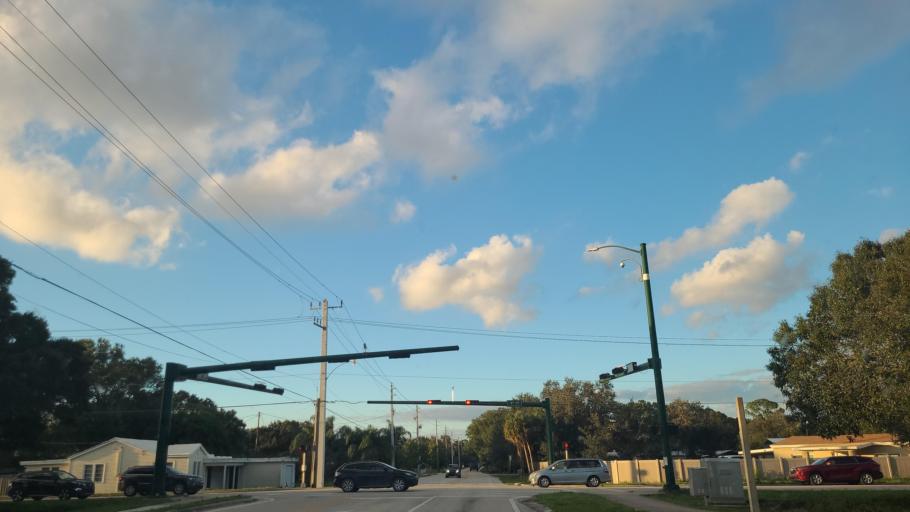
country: US
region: Florida
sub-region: Indian River County
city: Vero Beach South
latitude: 27.6159
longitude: -80.4059
